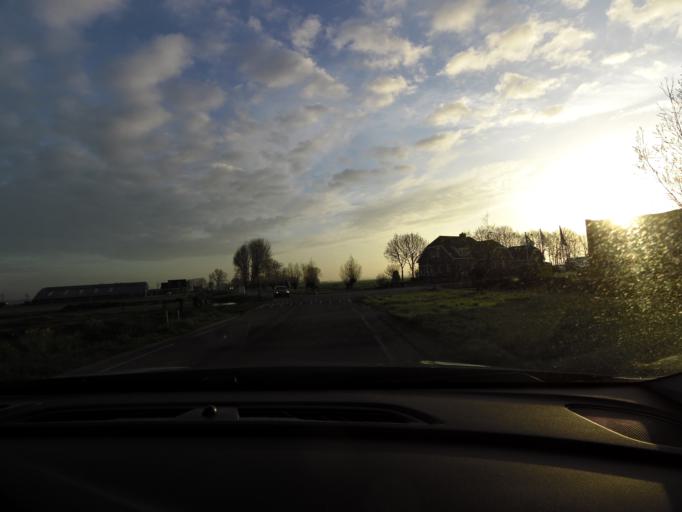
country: NL
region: South Holland
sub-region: Gemeente Gorinchem
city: Gorinchem
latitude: 51.8855
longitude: 4.9473
